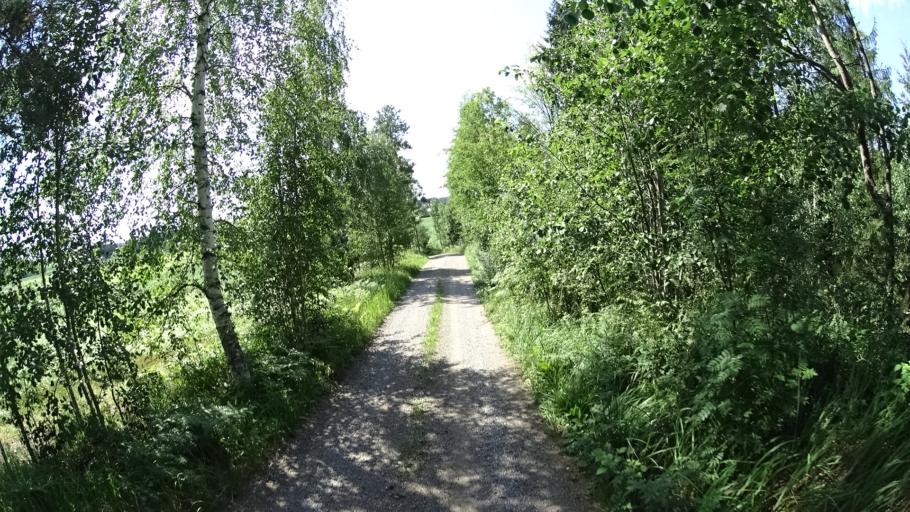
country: FI
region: Haeme
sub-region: Forssa
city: Tammela
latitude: 60.7640
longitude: 23.8873
